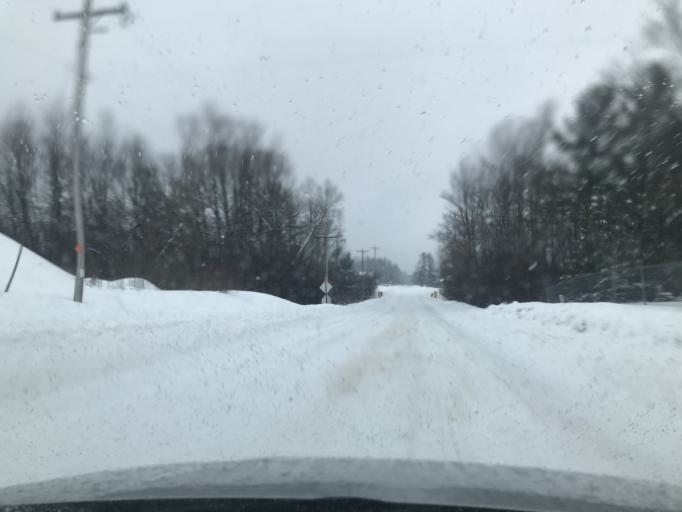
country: US
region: Wisconsin
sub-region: Marinette County
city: Peshtigo
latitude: 45.3809
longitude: -87.9469
